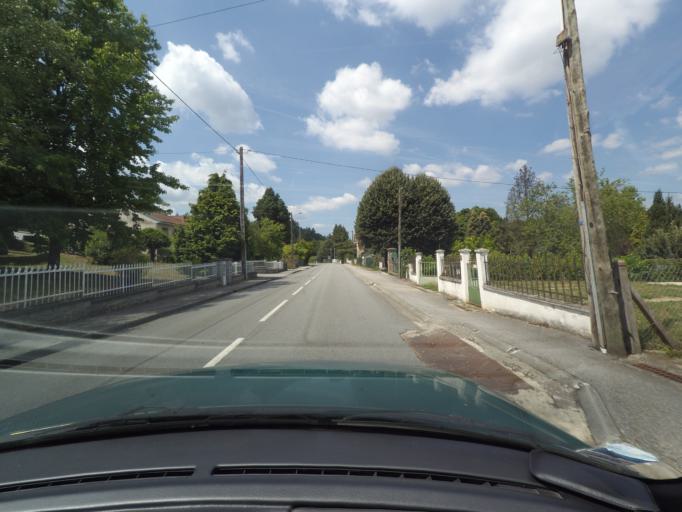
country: FR
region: Limousin
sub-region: Departement de la Haute-Vienne
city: Bosmie-l'Aiguille
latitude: 45.7744
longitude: 1.2141
